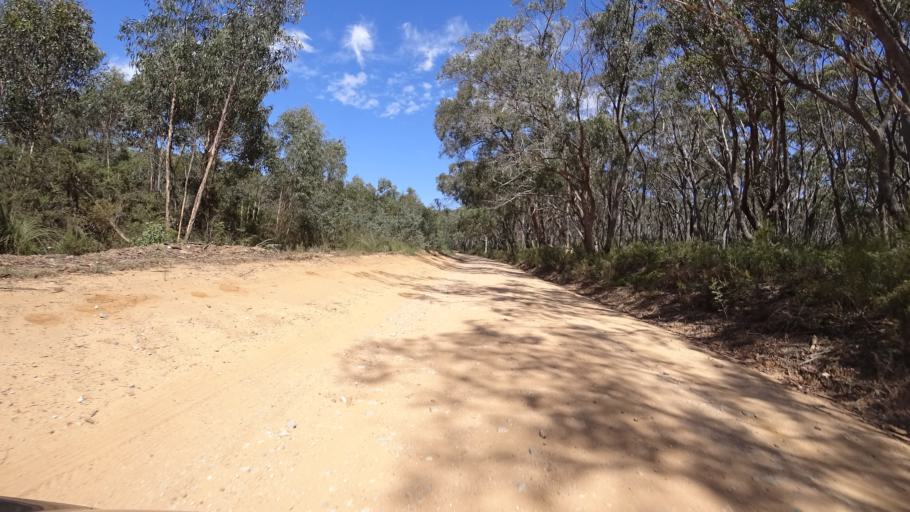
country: AU
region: New South Wales
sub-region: Lithgow
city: Lithgow
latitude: -33.3339
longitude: 150.2495
